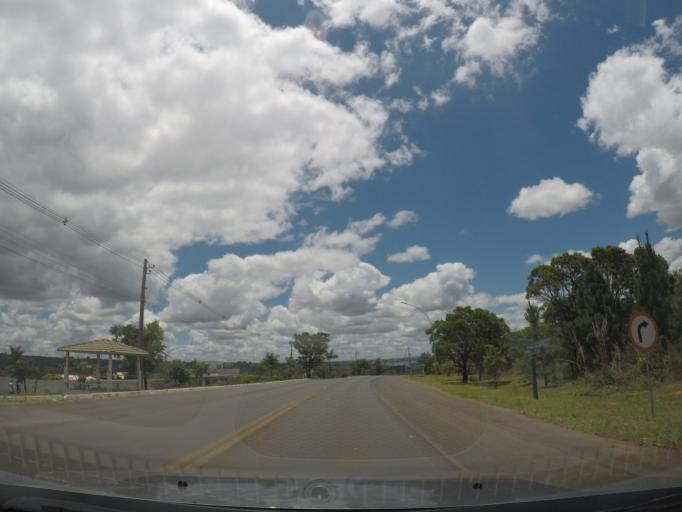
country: BR
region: Federal District
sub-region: Brasilia
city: Brasilia
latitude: -15.7849
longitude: -47.7994
